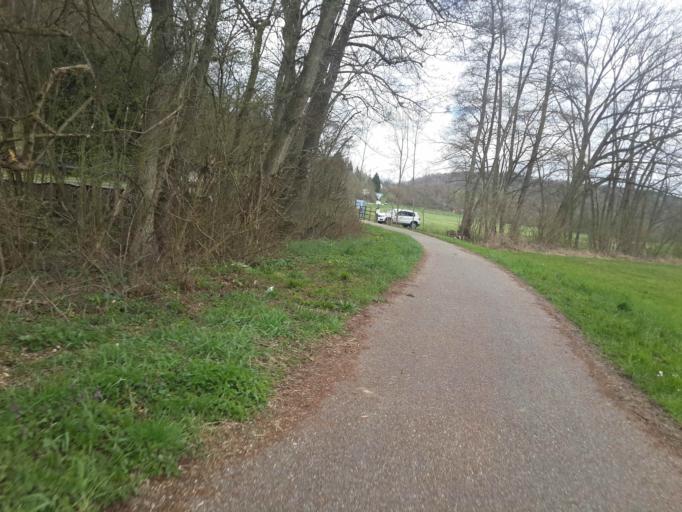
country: DE
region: Baden-Wuerttemberg
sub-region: Regierungsbezirk Stuttgart
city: Oedheim
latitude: 49.2713
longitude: 9.2203
